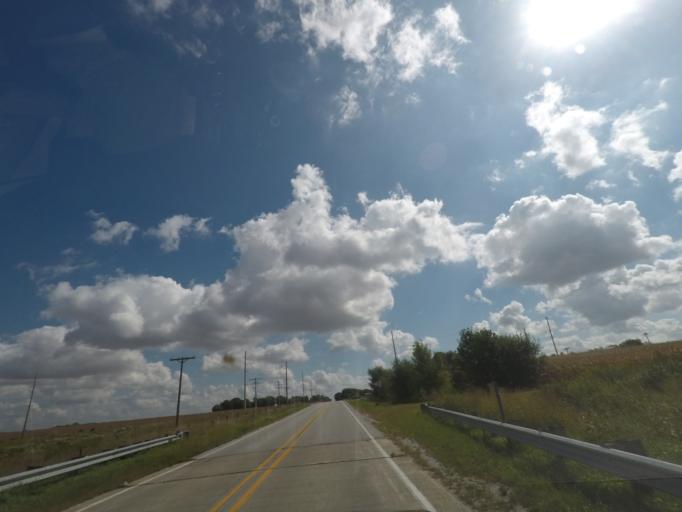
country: US
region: Iowa
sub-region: Story County
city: Nevada
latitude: 42.0225
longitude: -93.3303
